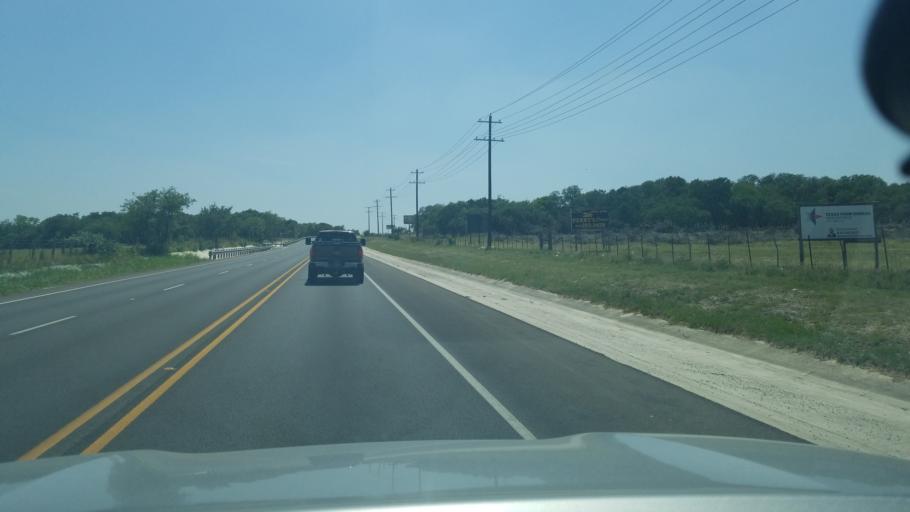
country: US
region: Texas
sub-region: Bexar County
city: Fair Oaks Ranch
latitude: 29.7995
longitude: -98.6643
